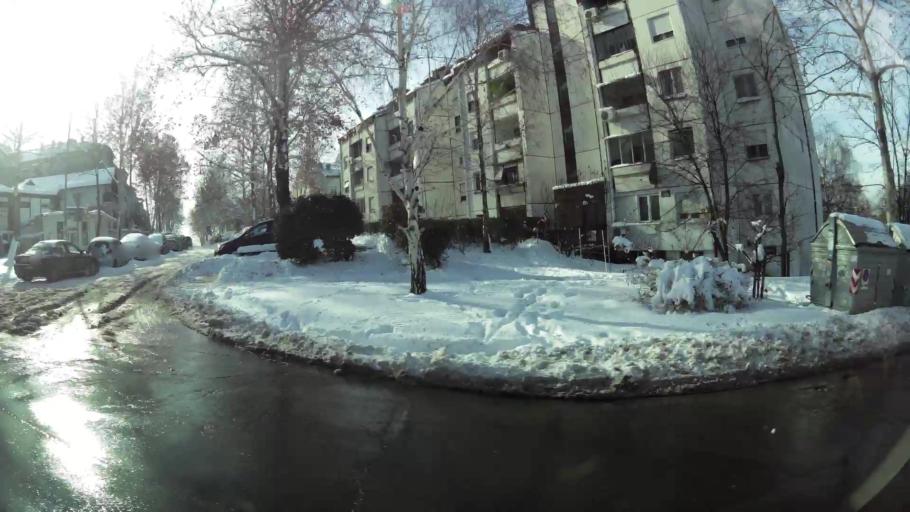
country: RS
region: Central Serbia
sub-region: Belgrade
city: Zvezdara
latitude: 44.7895
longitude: 20.5423
